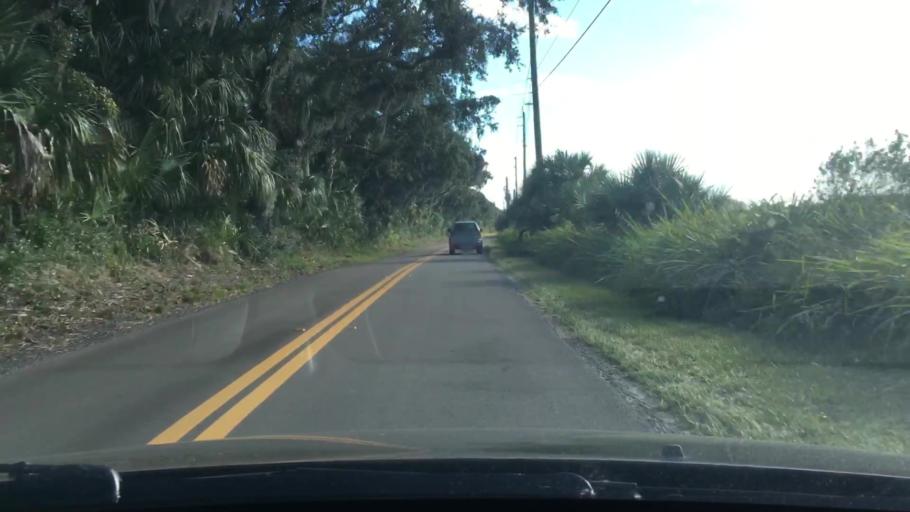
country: US
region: Florida
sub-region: Volusia County
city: Ormond-by-the-Sea
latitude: 29.3937
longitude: -81.0913
